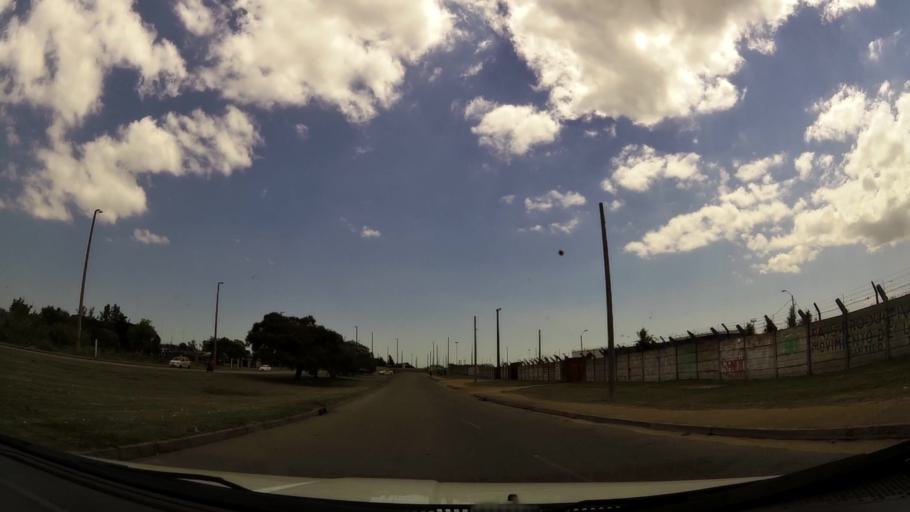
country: UY
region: Canelones
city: La Paz
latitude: -34.8228
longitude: -56.2422
